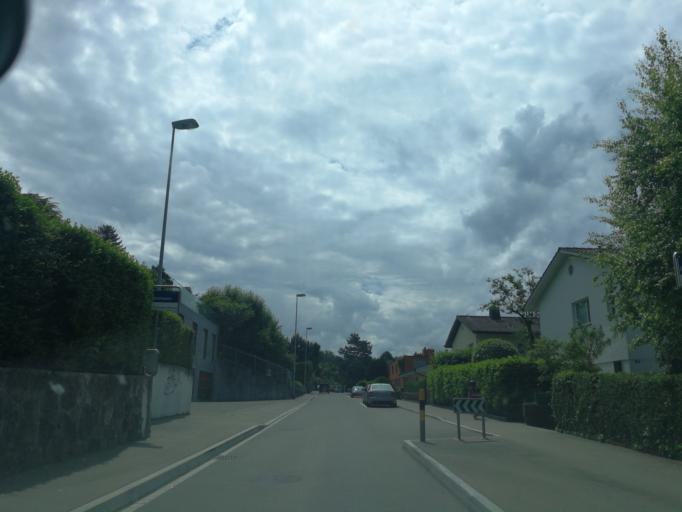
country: CH
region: Zurich
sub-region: Bezirk Meilen
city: Erlenbach / links des Dorfbachs oberhalb Bahnlinie
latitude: 47.2993
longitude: 8.6021
